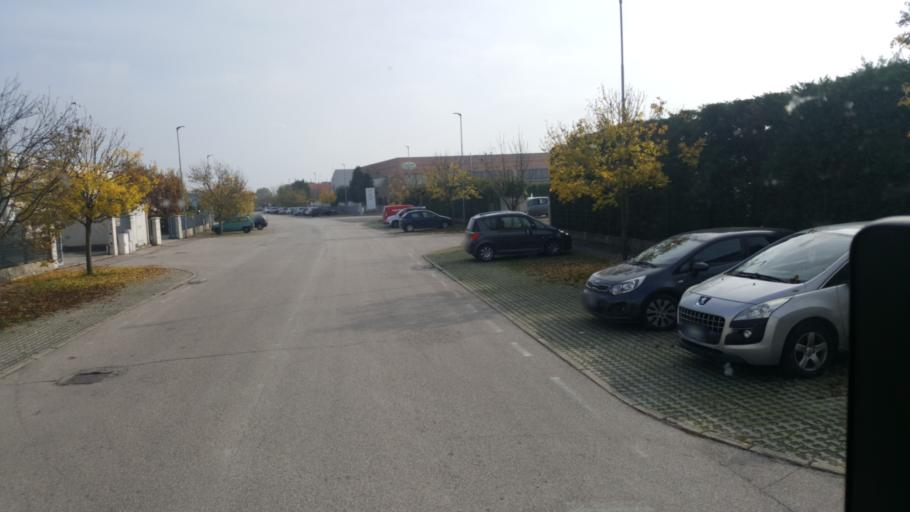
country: IT
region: Lombardy
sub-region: Provincia di Mantova
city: Suzzara
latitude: 44.9937
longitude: 10.7662
